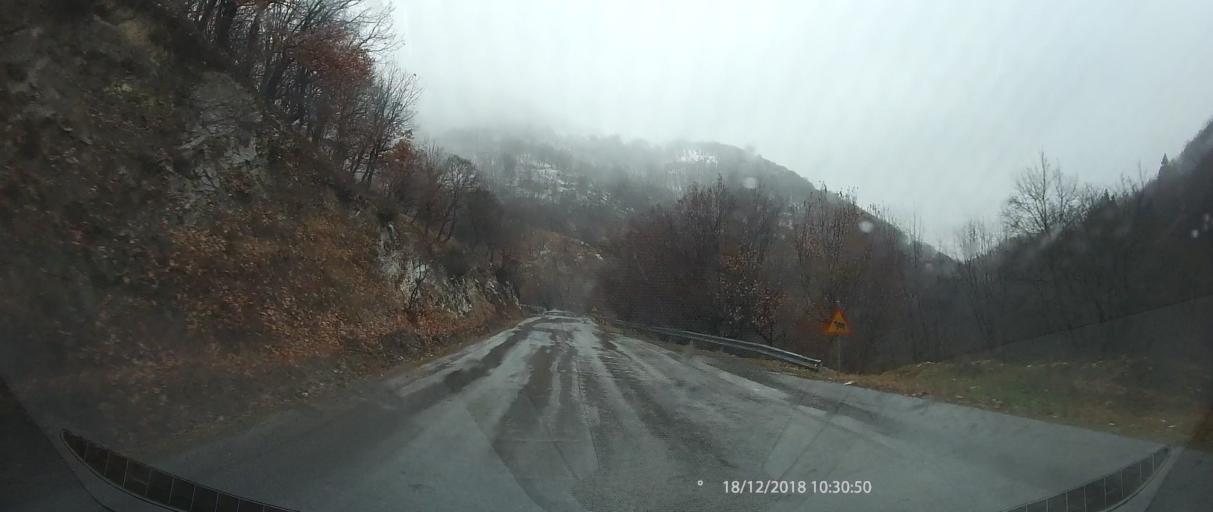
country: GR
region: Central Macedonia
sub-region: Nomos Pierias
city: Kato Milia
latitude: 40.1905
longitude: 22.2798
